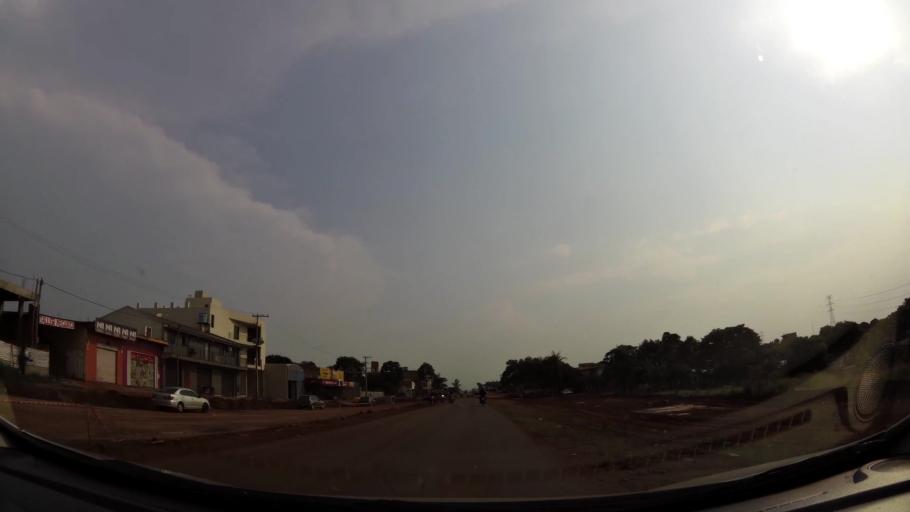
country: PY
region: Alto Parana
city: Ciudad del Este
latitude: -25.4814
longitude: -54.6580
